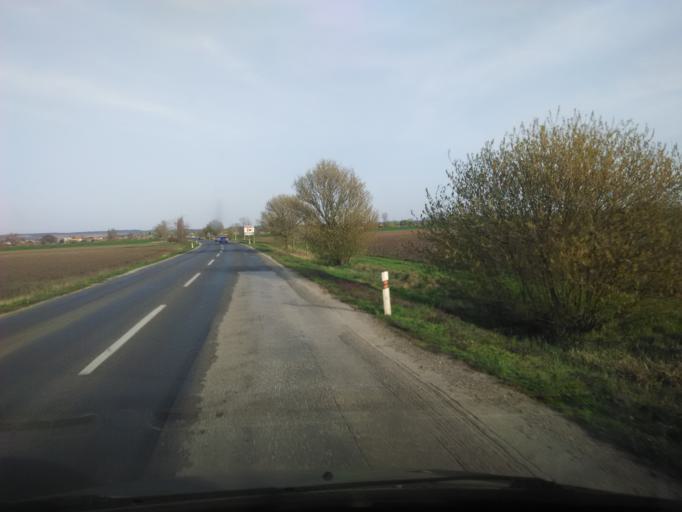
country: SK
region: Nitriansky
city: Surany
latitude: 48.0958
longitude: 18.2473
